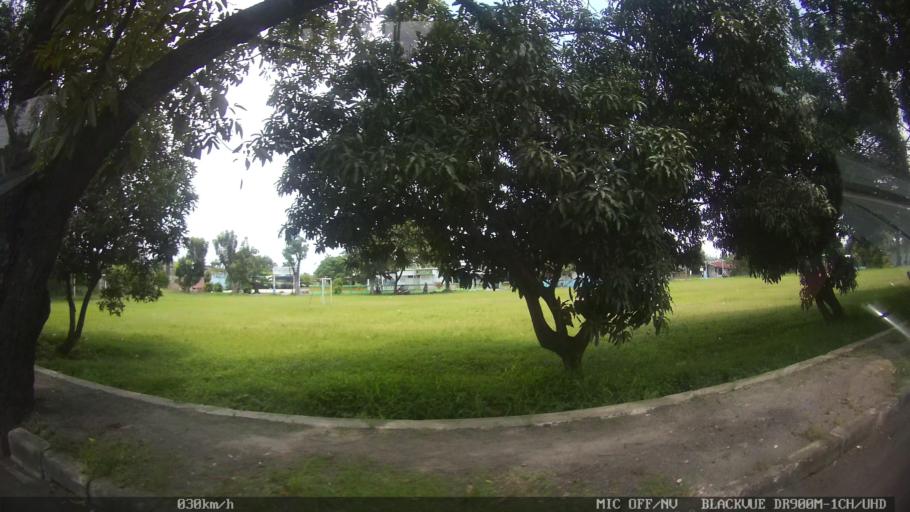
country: ID
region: North Sumatra
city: Labuhan Deli
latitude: 3.6788
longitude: 98.6653
